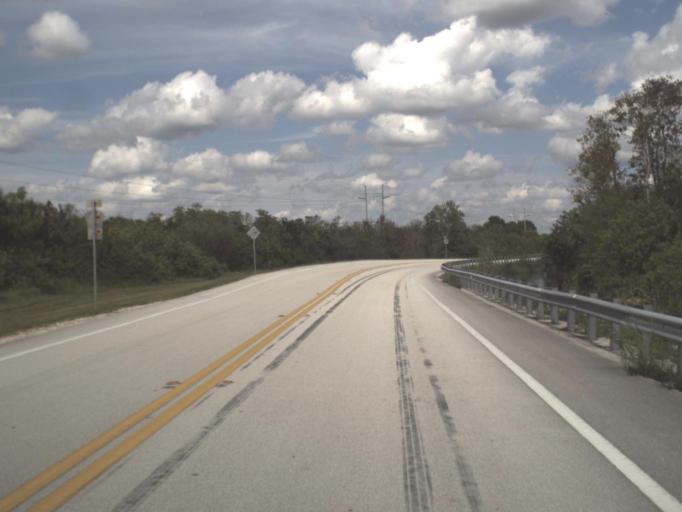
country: US
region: Florida
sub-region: Collier County
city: Lely Resort
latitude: 25.9467
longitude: -81.3580
